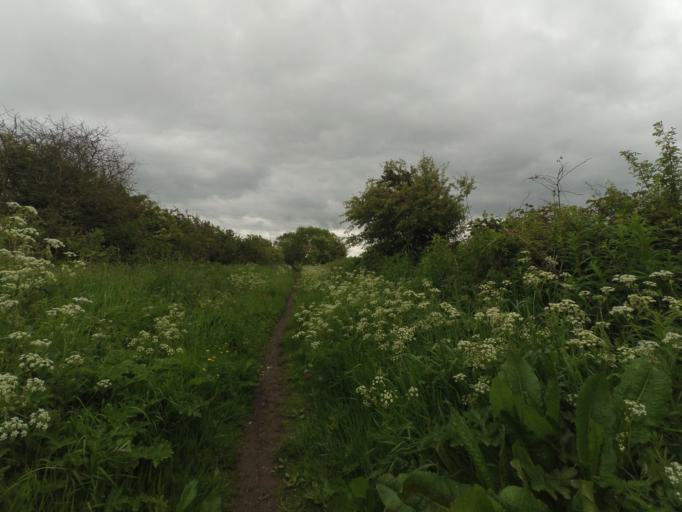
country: GB
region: Scotland
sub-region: East Lothian
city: Tranent
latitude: 55.9254
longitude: -2.9782
